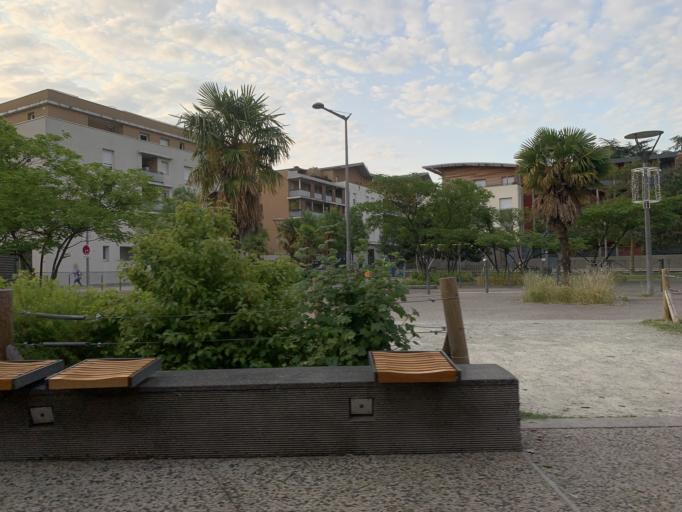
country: FR
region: Rhone-Alpes
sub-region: Departement du Rhone
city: Decines-Charpieu
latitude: 45.7717
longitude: 4.9560
